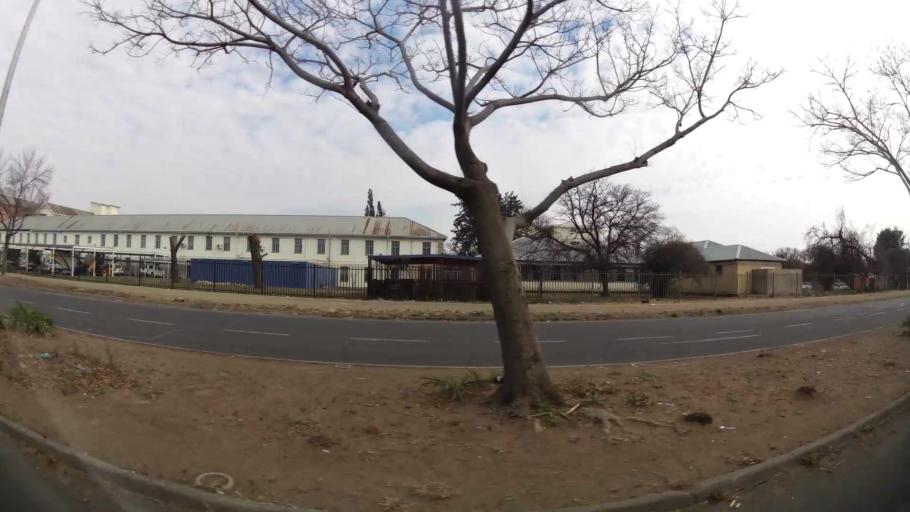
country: ZA
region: Orange Free State
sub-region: Mangaung Metropolitan Municipality
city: Bloemfontein
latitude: -29.1284
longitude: 26.2082
